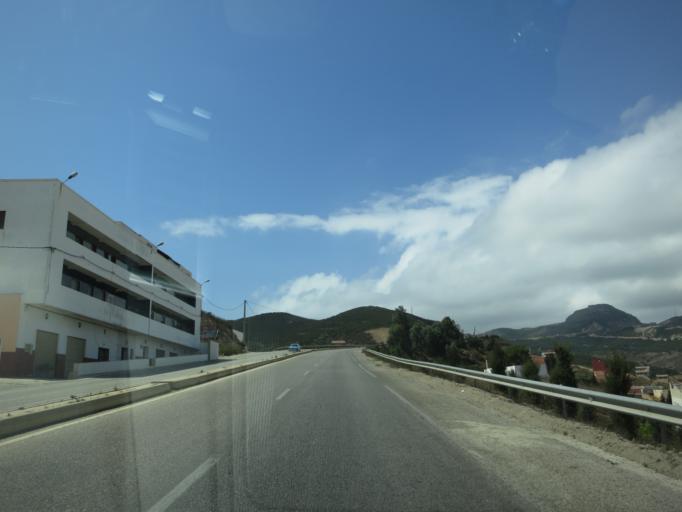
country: ES
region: Ceuta
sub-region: Ceuta
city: Ceuta
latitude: 35.8698
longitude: -5.3670
